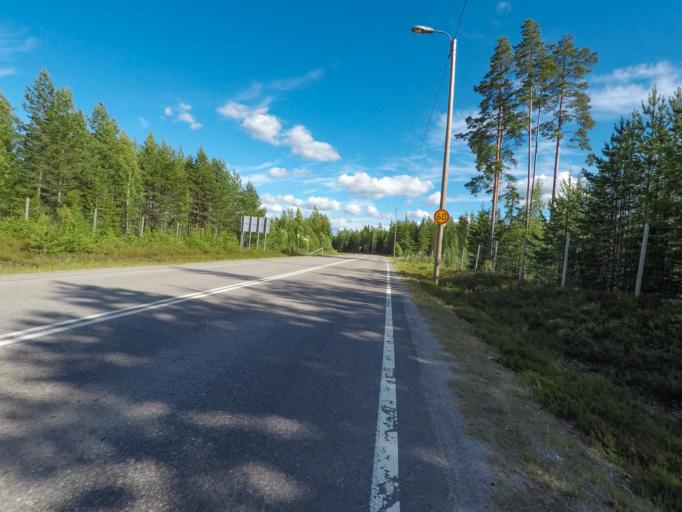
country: FI
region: South Karelia
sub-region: Lappeenranta
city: Joutseno
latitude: 61.1481
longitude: 28.6168
